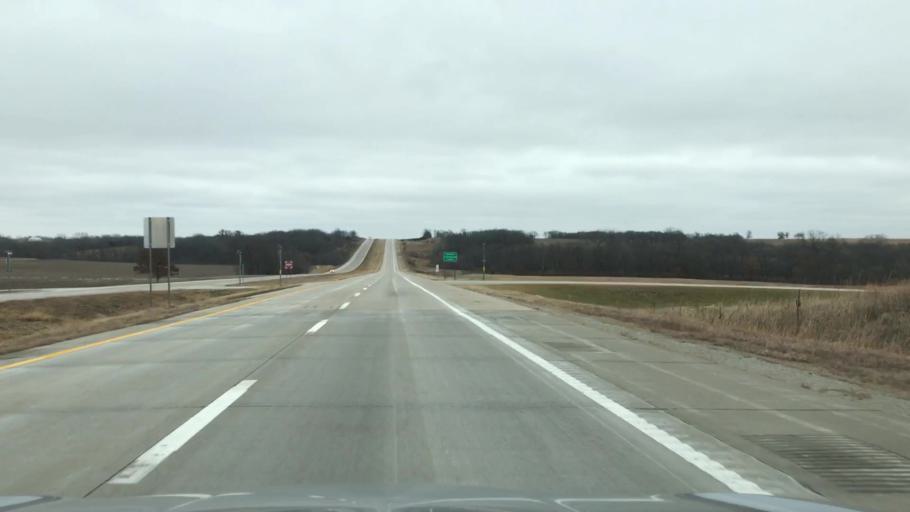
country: US
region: Missouri
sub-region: Livingston County
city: Chillicothe
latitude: 39.7351
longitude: -93.7599
